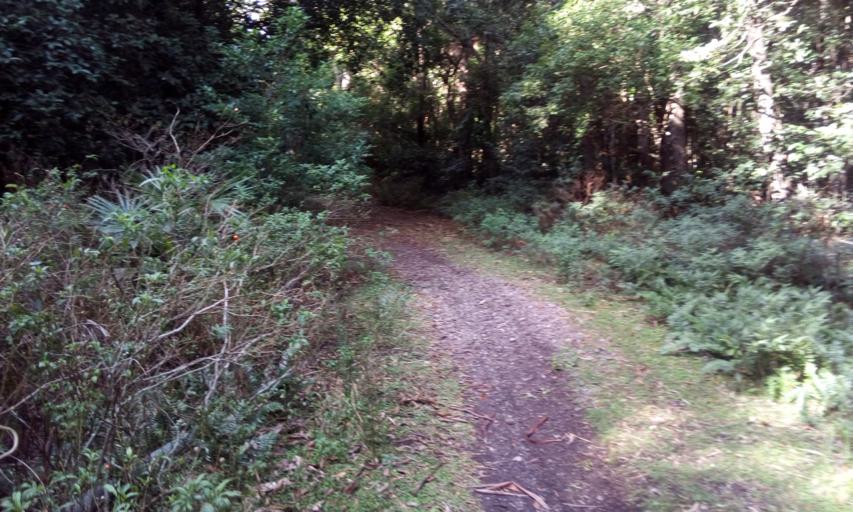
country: AU
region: New South Wales
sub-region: Wollongong
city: Cordeaux Heights
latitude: -34.4453
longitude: 150.8062
